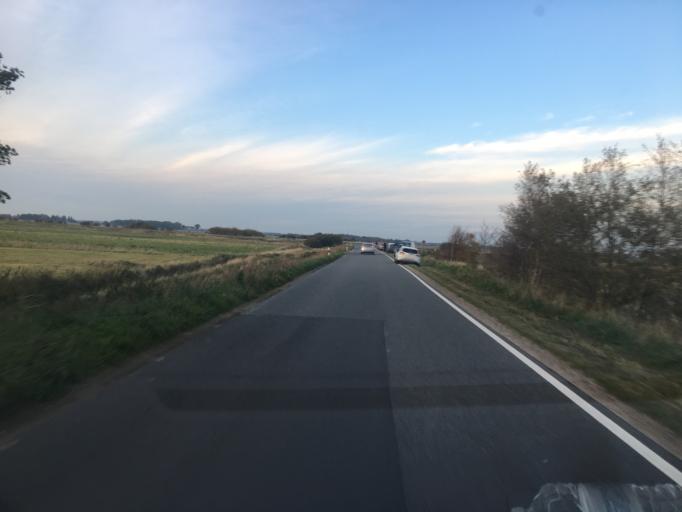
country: DE
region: Schleswig-Holstein
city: Aventoft
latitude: 54.8946
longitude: 8.8483
